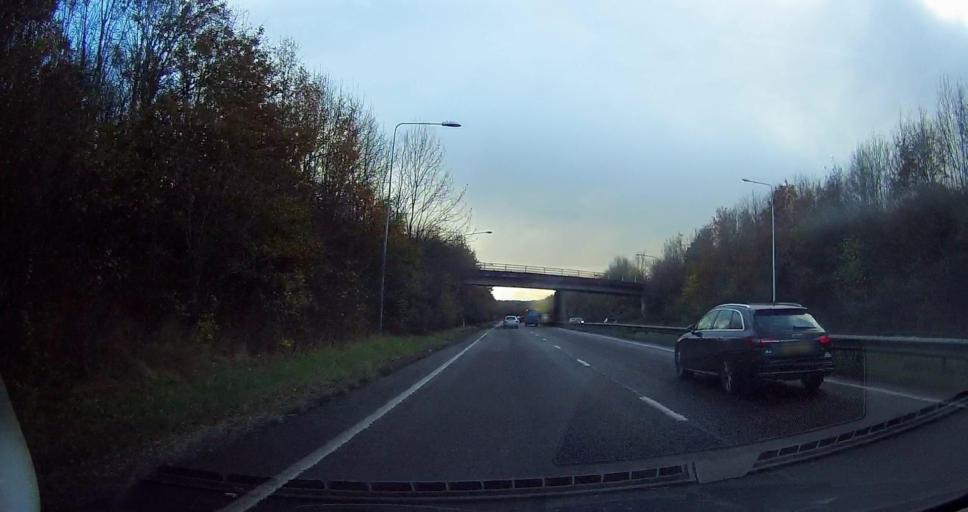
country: GB
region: England
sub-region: West Sussex
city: Hurstpierpoint
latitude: 50.9552
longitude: -0.1932
